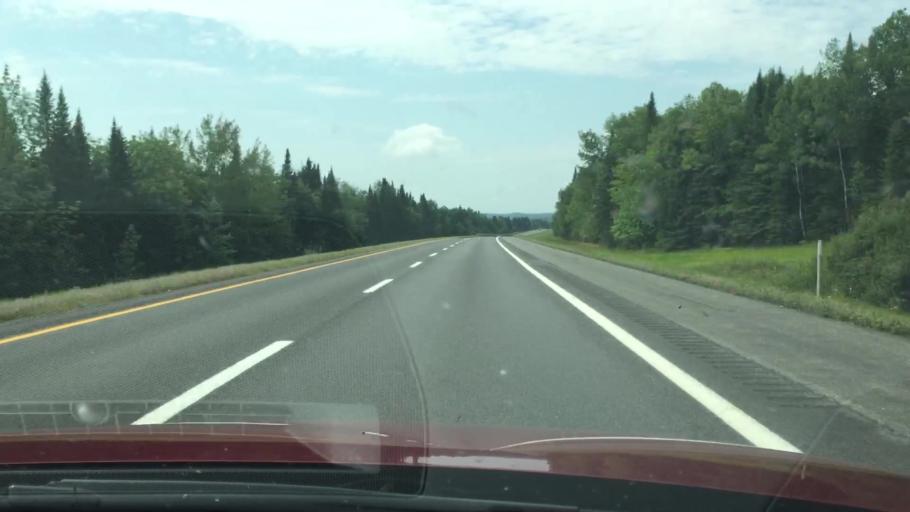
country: US
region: Maine
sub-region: Aroostook County
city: Hodgdon
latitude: 46.1204
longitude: -68.1182
